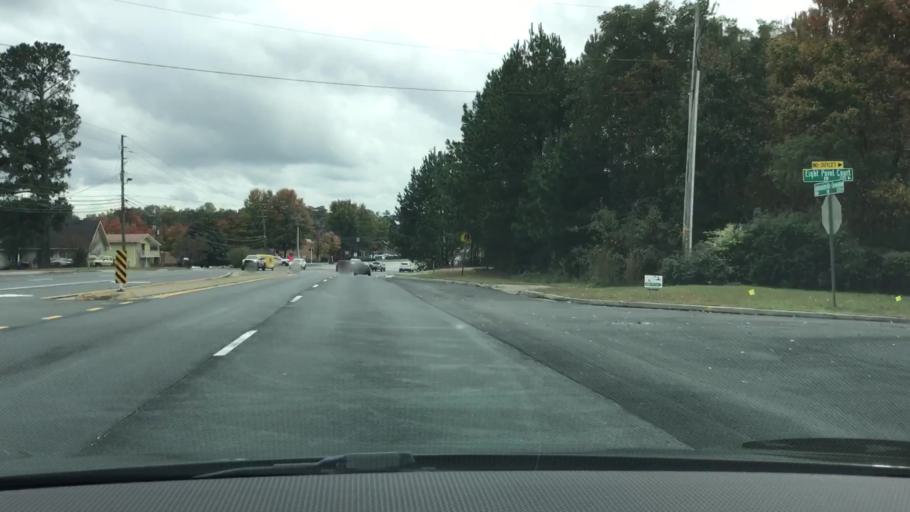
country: US
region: Georgia
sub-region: Gwinnett County
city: Suwanee
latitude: 34.0060
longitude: -84.0415
